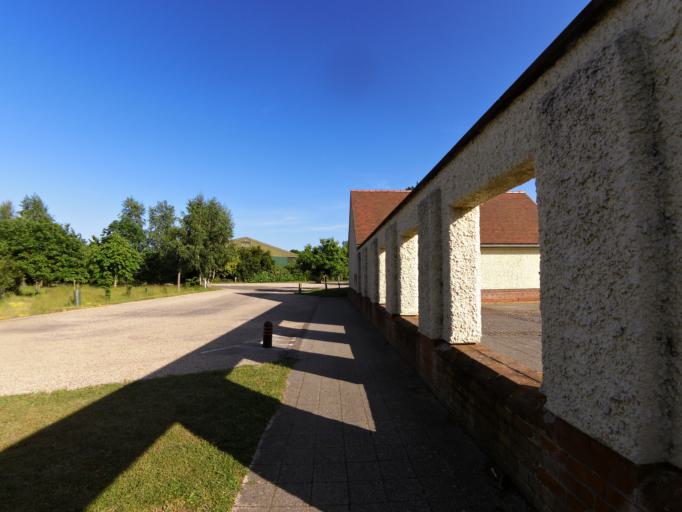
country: GB
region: England
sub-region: Suffolk
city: Woodbridge
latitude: 52.0947
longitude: 1.3415
